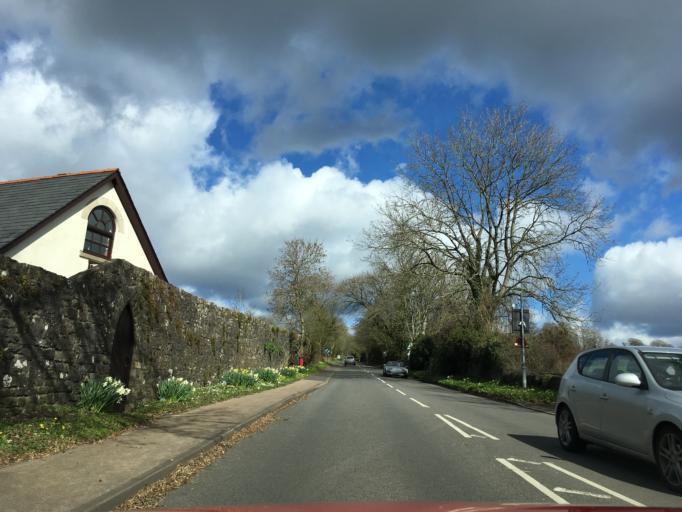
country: GB
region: Wales
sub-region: Monmouthshire
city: Chepstow
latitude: 51.6653
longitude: -2.6972
